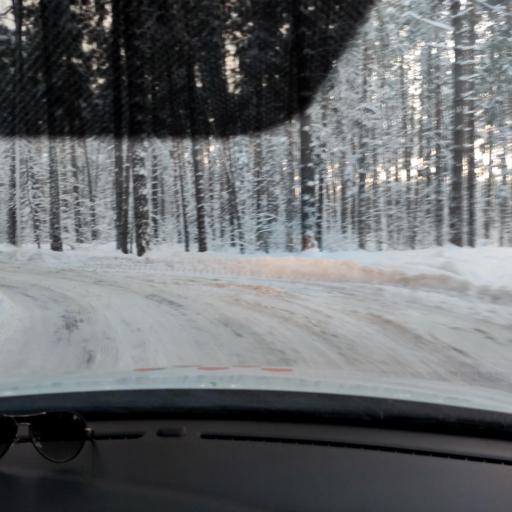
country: RU
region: Tatarstan
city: Verkhniy Uslon
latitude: 55.6417
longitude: 49.0211
